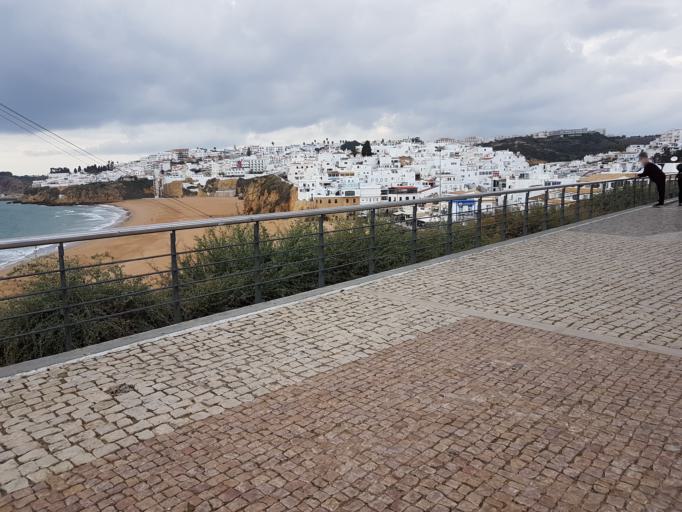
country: PT
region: Faro
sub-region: Albufeira
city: Albufeira
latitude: 37.0866
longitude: -8.2479
